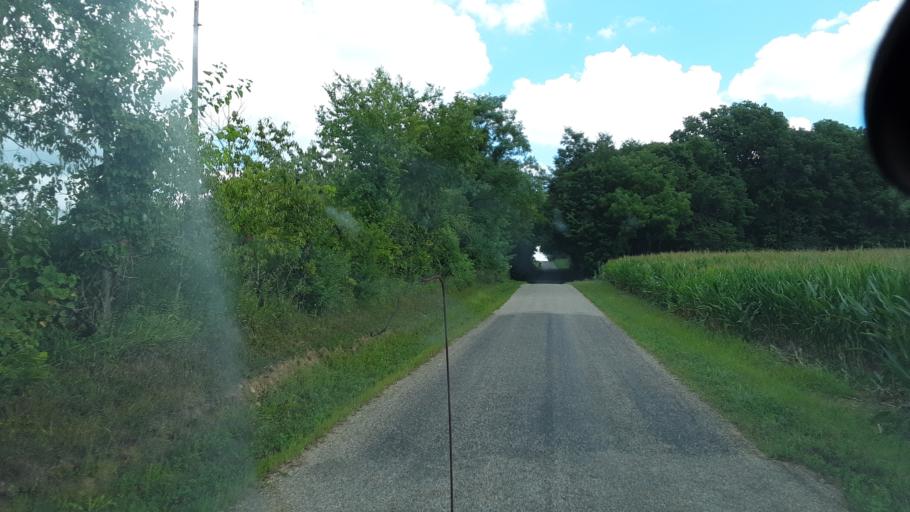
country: US
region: Ohio
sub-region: Licking County
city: Utica
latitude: 40.2619
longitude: -82.4132
